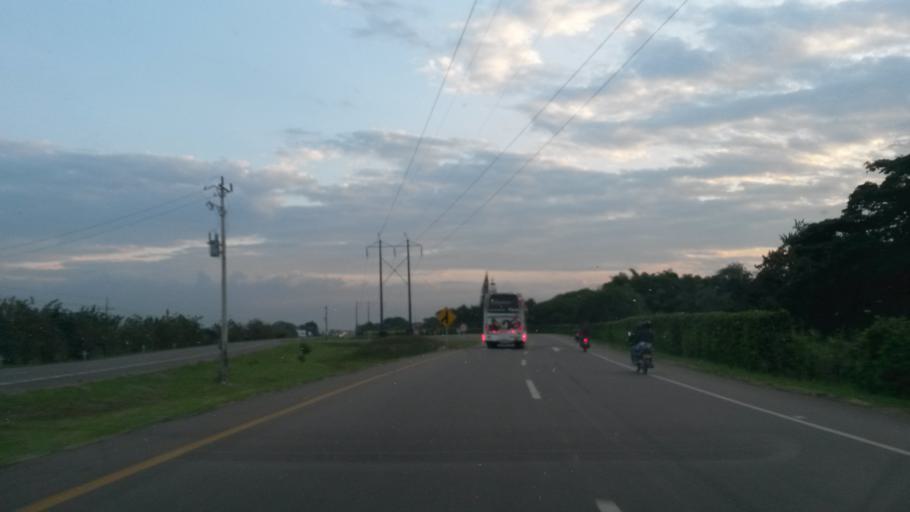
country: CO
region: Cauca
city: Caloto
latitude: 3.1162
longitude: -76.4663
